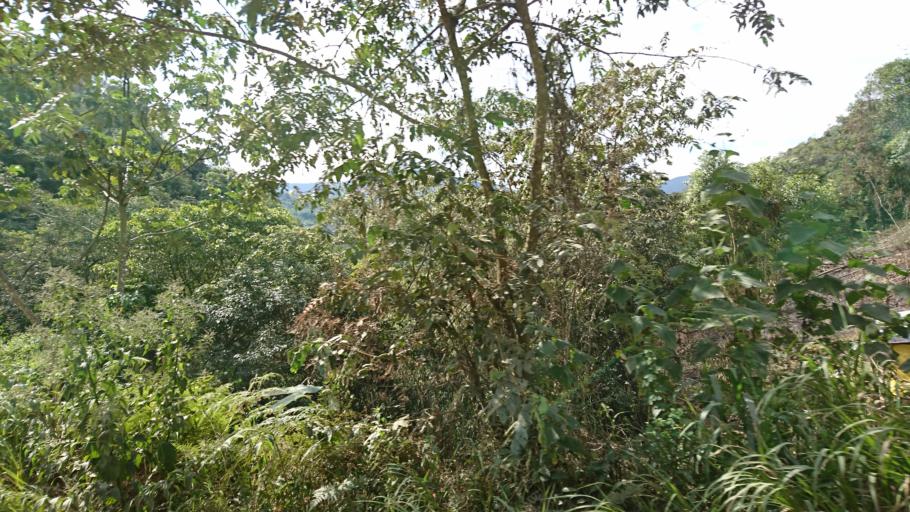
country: BO
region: La Paz
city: Coroico
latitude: -16.0849
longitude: -67.7902
